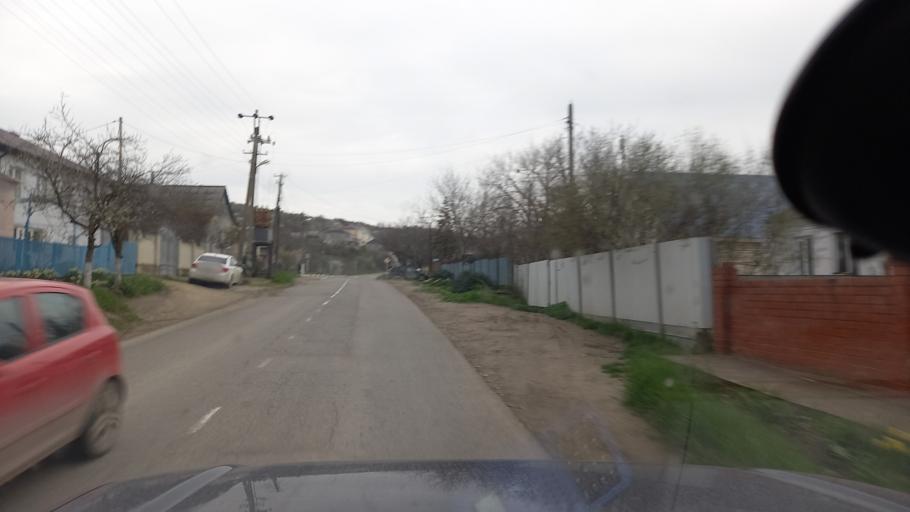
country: RU
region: Krasnodarskiy
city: Sukko
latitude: 44.8486
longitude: 37.4359
